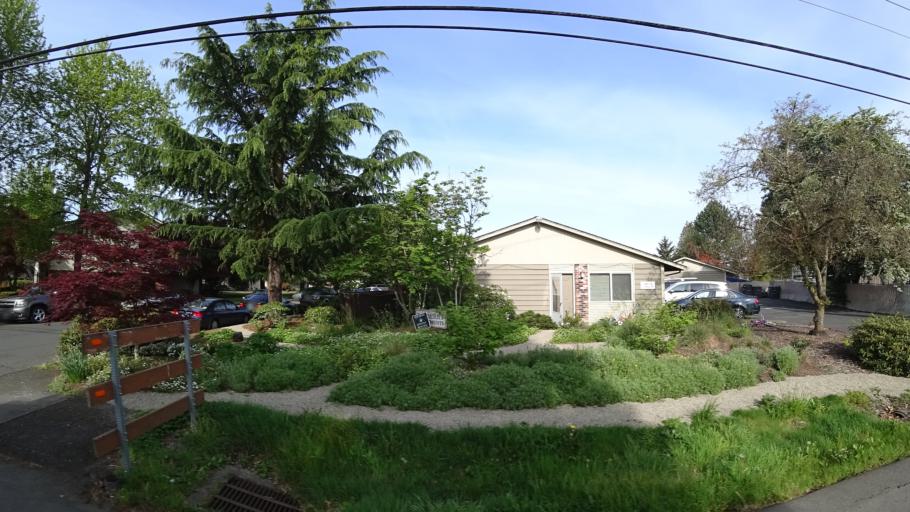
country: US
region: Oregon
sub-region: Washington County
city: Hillsboro
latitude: 45.5323
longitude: -122.9646
